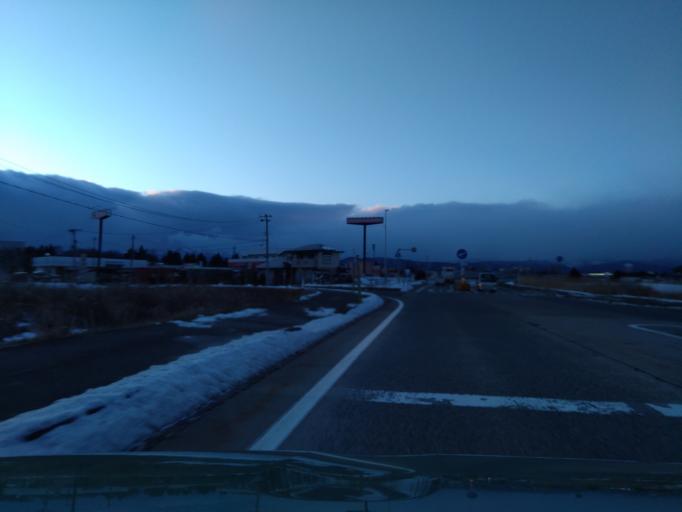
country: JP
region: Iwate
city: Shizukuishi
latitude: 39.6922
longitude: 140.9836
